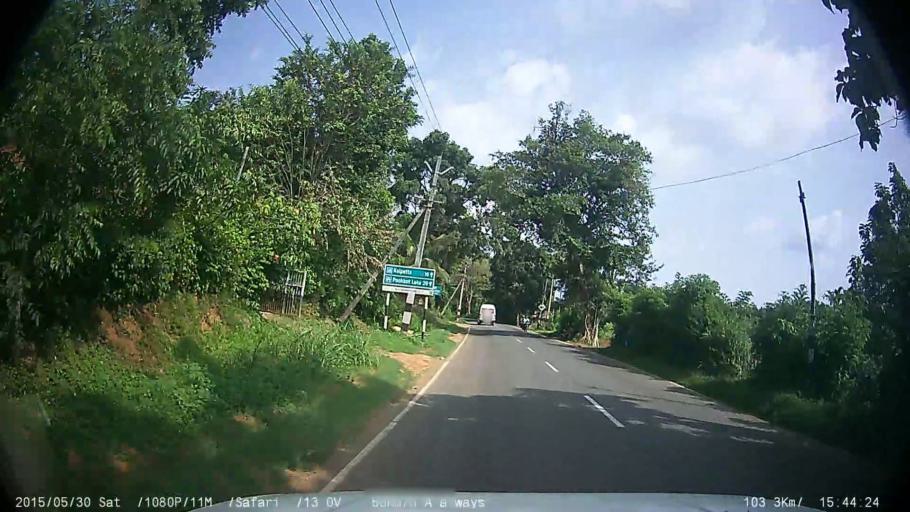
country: IN
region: Kerala
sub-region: Wayanad
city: Panamaram
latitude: 11.7250
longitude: 76.0779
